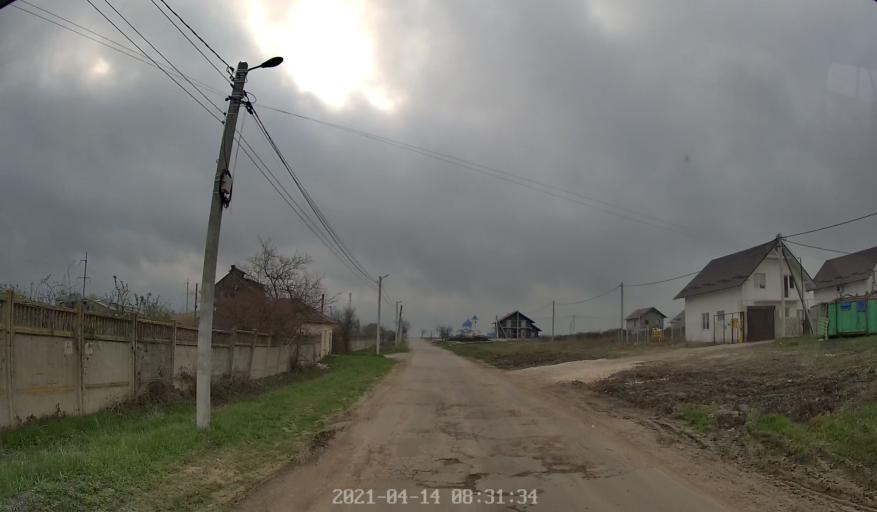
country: MD
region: Chisinau
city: Stauceni
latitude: 47.0609
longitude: 28.9353
